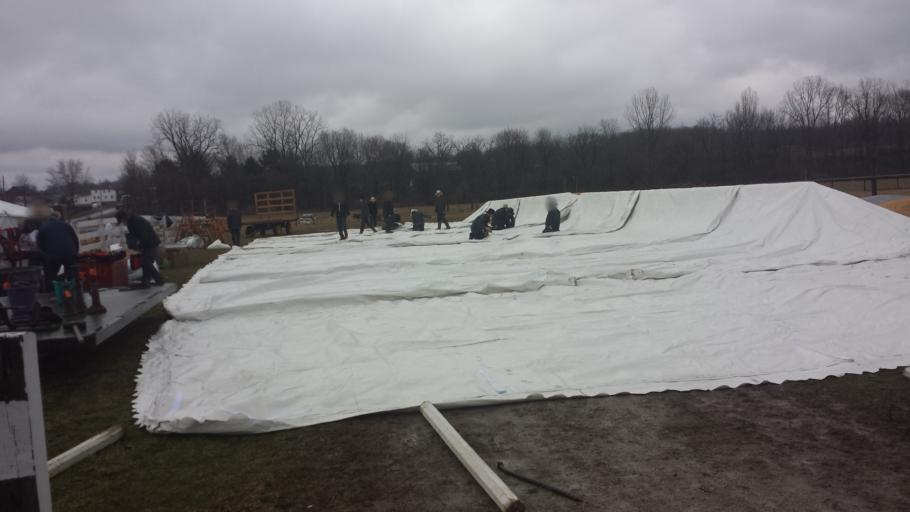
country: US
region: Ohio
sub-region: Richland County
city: Lexington
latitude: 40.6007
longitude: -82.6502
